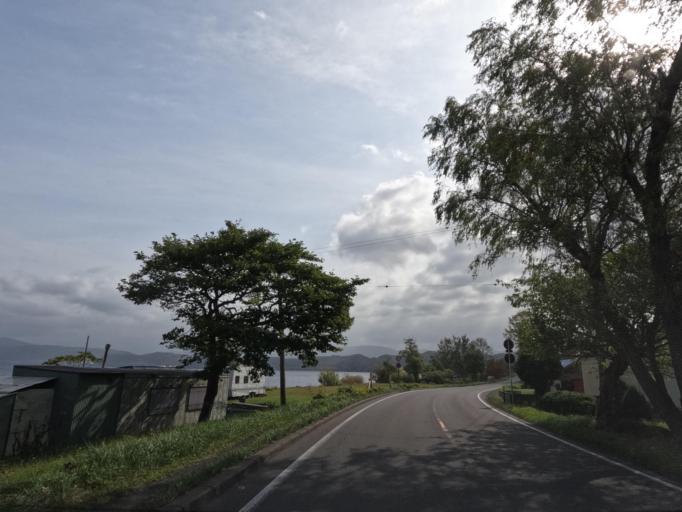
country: JP
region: Hokkaido
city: Date
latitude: 42.5636
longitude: 140.8443
